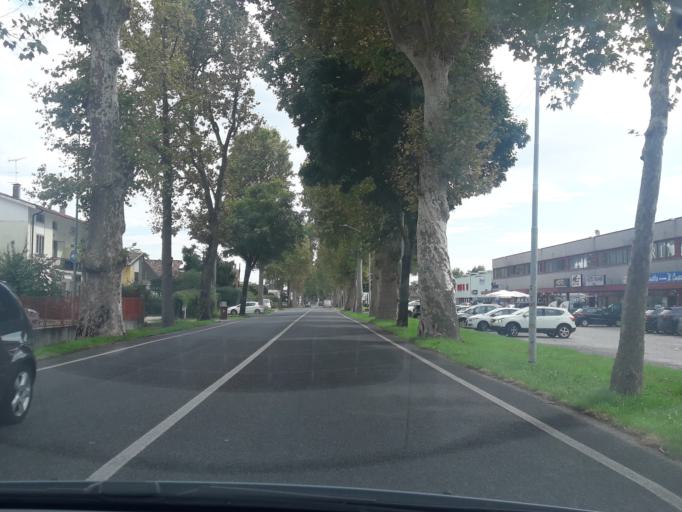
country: IT
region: Friuli Venezia Giulia
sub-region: Provincia di Udine
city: Udine
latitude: 46.0380
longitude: 13.2540
